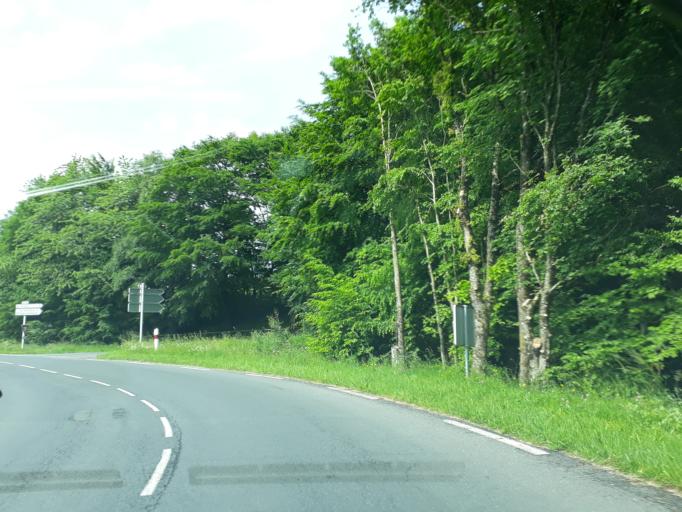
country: FR
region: Limousin
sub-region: Departement de la Correze
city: Beynat
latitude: 45.1228
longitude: 1.7879
